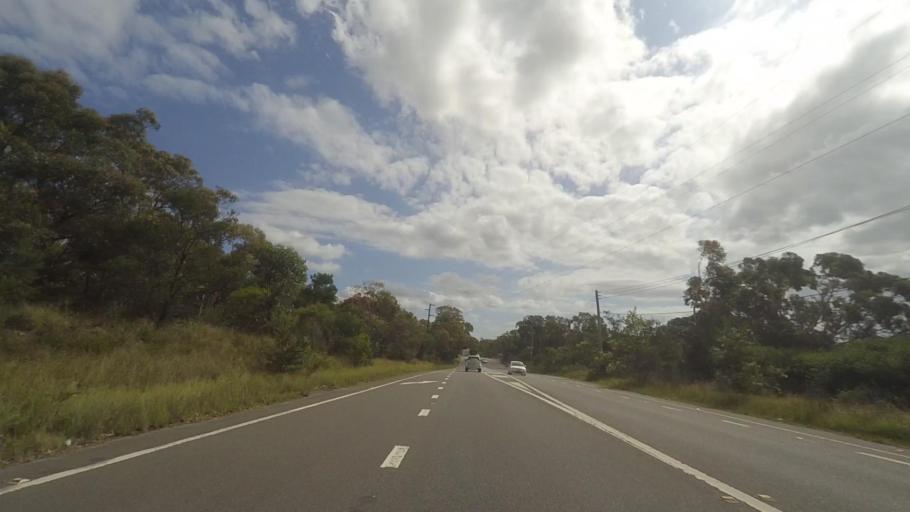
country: AU
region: New South Wales
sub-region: Sutherland Shire
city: Engadine
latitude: -34.0401
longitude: 150.9975
